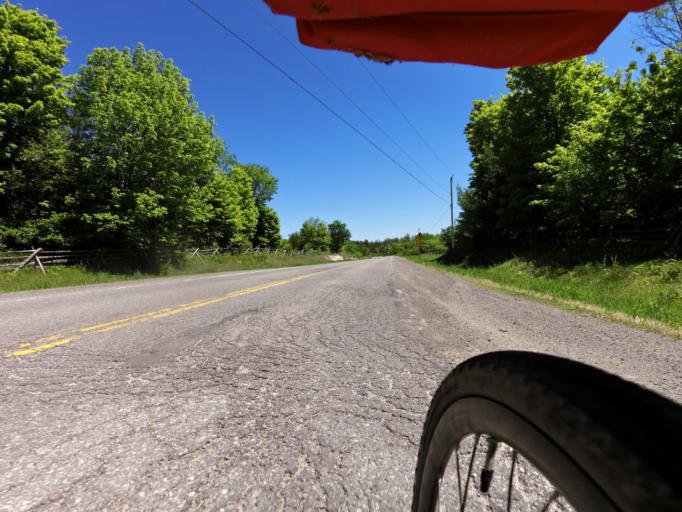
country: CA
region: Ontario
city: Carleton Place
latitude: 45.1839
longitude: -76.3659
